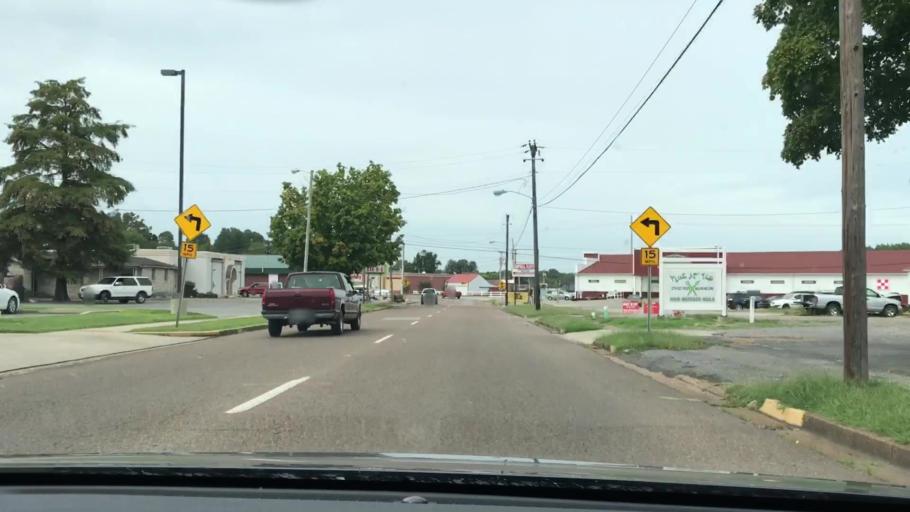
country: US
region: Kentucky
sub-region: Marshall County
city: Benton
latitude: 36.8628
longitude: -88.3500
